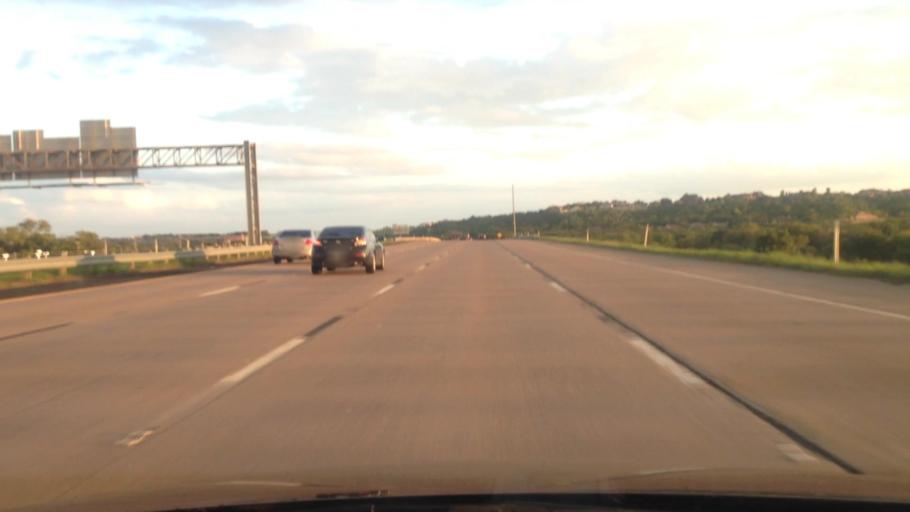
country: US
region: Texas
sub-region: Tarrant County
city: White Settlement
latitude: 32.7206
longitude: -97.4799
